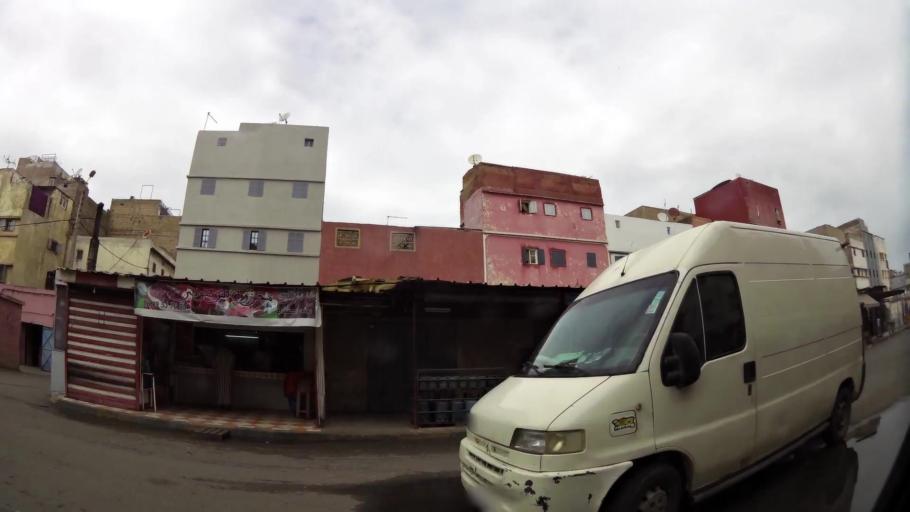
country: MA
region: Grand Casablanca
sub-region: Mediouna
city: Tit Mellil
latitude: 33.6118
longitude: -7.5084
